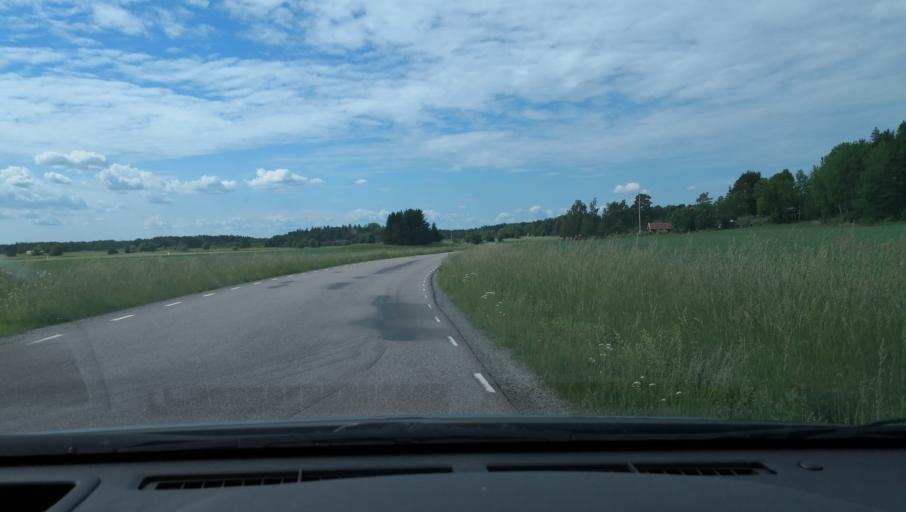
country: SE
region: Uppsala
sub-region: Uppsala Kommun
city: Uppsala
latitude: 59.8142
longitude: 17.5027
